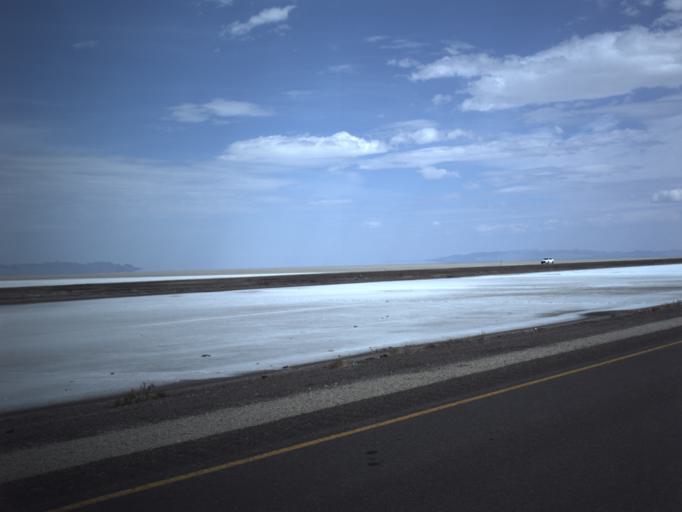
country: US
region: Utah
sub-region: Tooele County
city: Wendover
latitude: 40.7346
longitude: -113.6657
